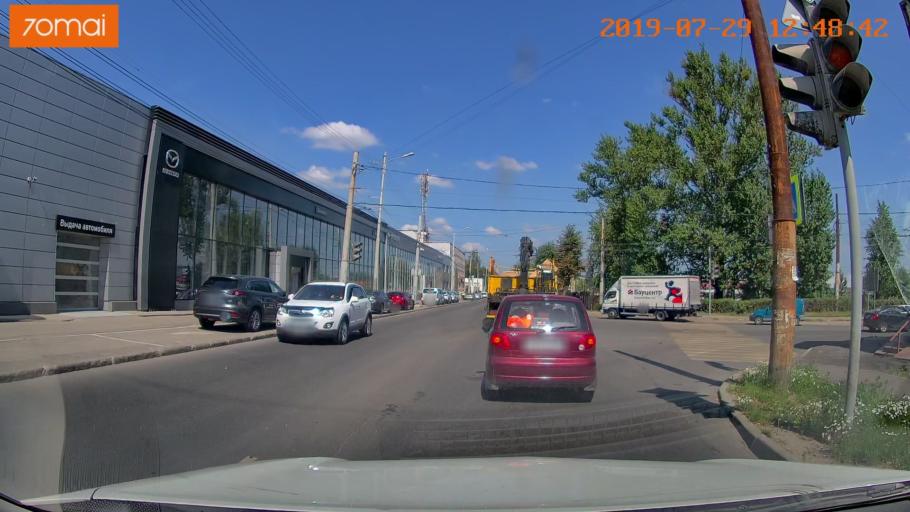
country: RU
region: Kaliningrad
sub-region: Gorod Kaliningrad
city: Kaliningrad
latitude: 54.6830
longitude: 20.5342
